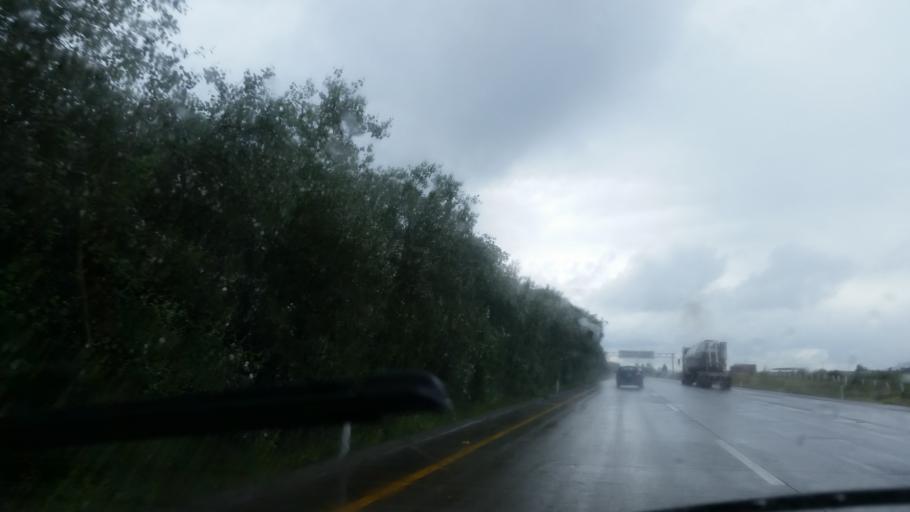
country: MX
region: Mexico
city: San Francisco Soyaniquilpan
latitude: 19.9890
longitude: -99.4562
